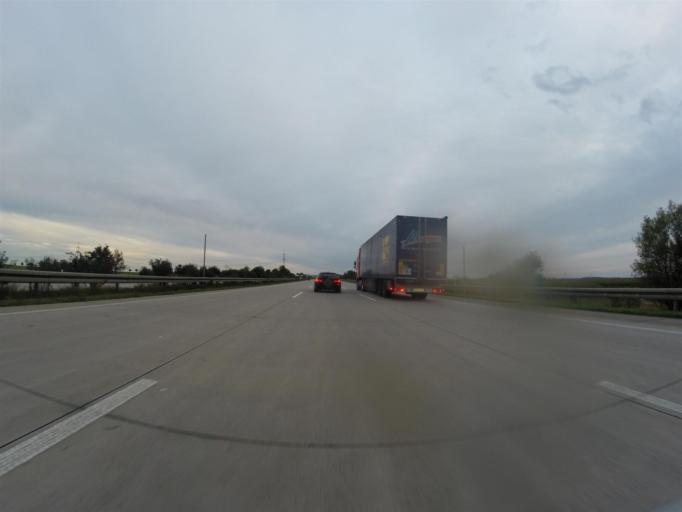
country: DE
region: Thuringia
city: Walpernhain
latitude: 51.0294
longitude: 11.9366
